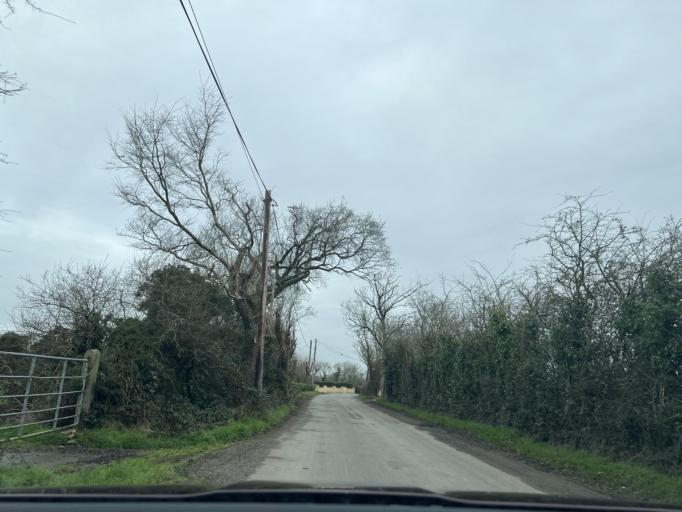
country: IE
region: Leinster
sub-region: Loch Garman
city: Castlebridge
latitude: 52.3783
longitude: -6.5248
